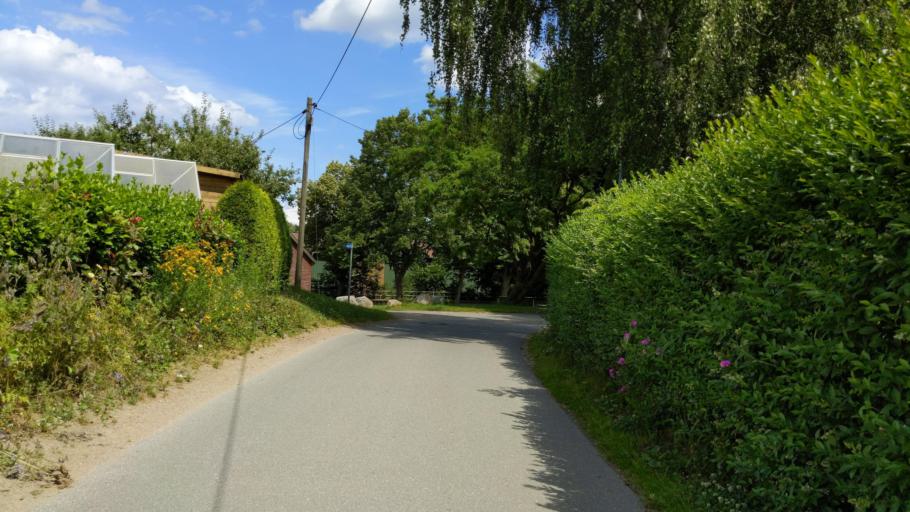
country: DE
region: Mecklenburg-Vorpommern
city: Kalkhorst
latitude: 53.9999
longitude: 11.0848
